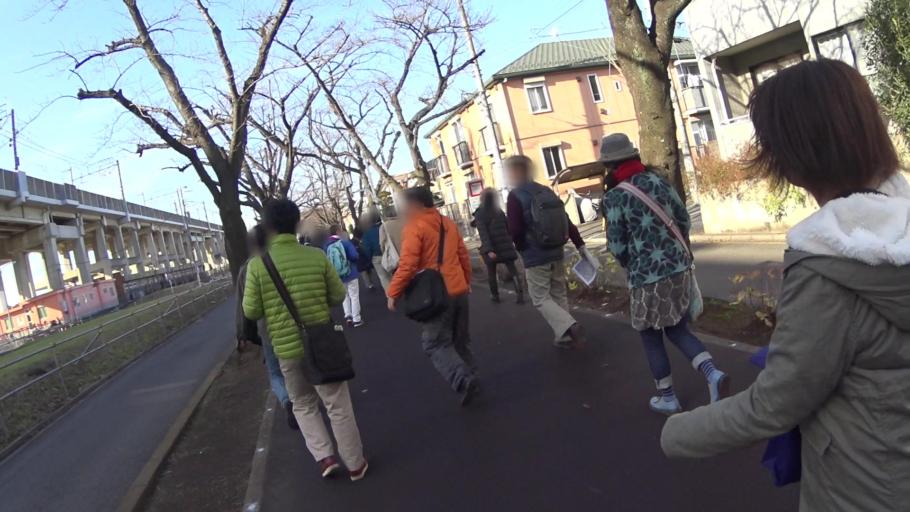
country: JP
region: Saitama
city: Yono
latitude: 35.8497
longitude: 139.6436
